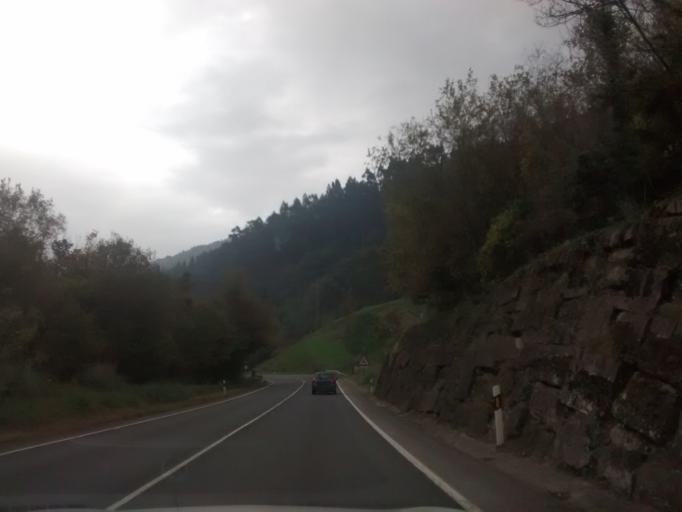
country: ES
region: Cantabria
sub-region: Provincia de Cantabria
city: Santiurde de Toranzo
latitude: 43.1836
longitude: -3.9105
